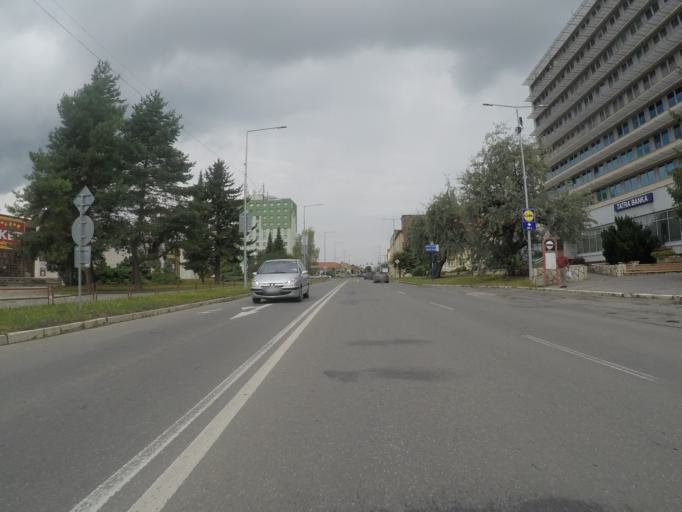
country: SK
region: Kosicky
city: Spisska Nova Ves
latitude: 48.9460
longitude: 20.5611
